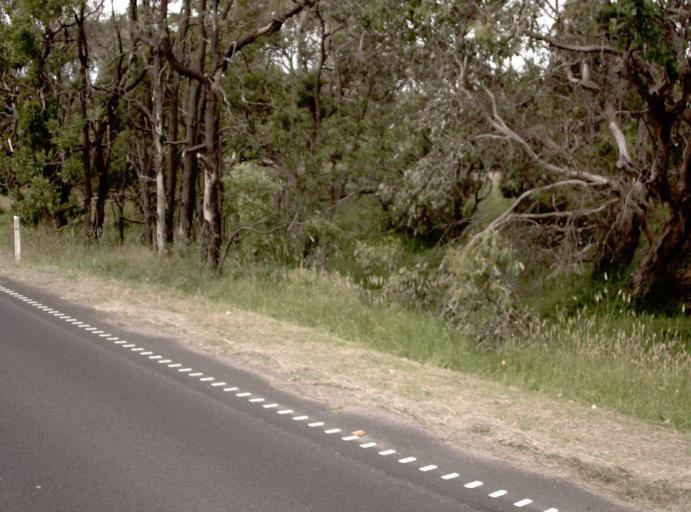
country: AU
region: Victoria
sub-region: Mornington Peninsula
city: Moorooduc
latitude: -38.2367
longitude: 145.0871
